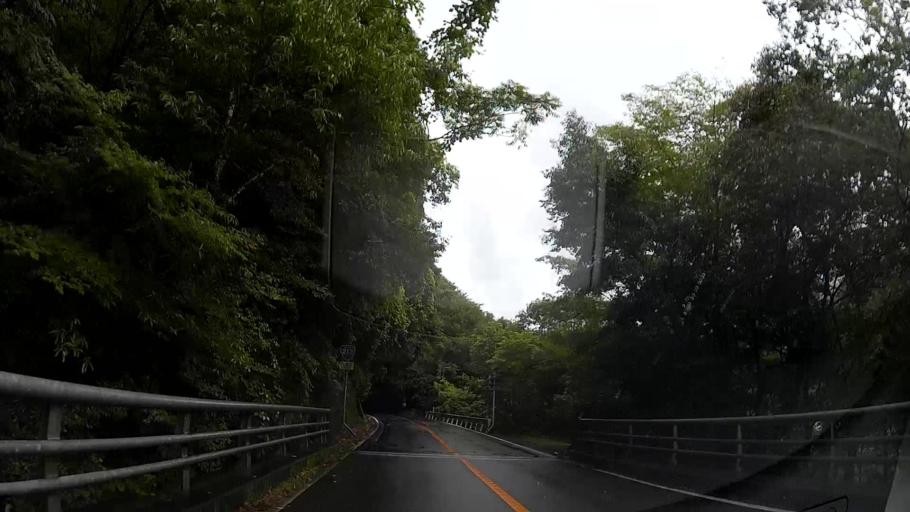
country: JP
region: Oita
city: Hita
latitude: 33.1916
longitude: 130.9946
